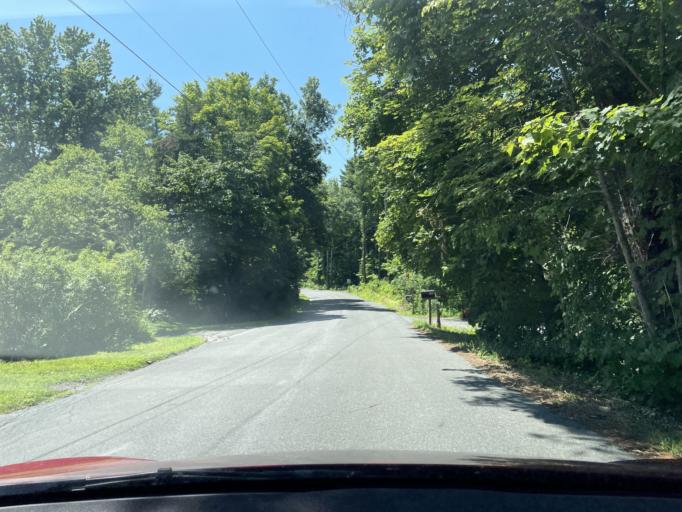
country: US
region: New York
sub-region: Ulster County
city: Lake Katrine
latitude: 42.0143
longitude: -73.9771
